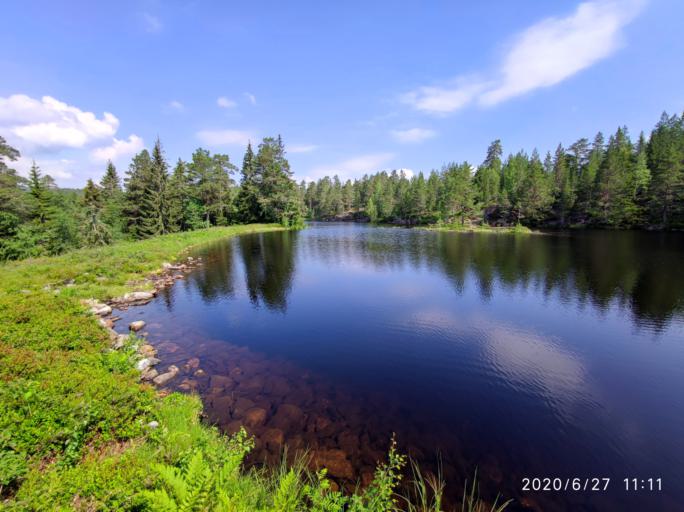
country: NO
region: Buskerud
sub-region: Kongsberg
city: Kongsberg
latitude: 59.6579
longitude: 9.5851
